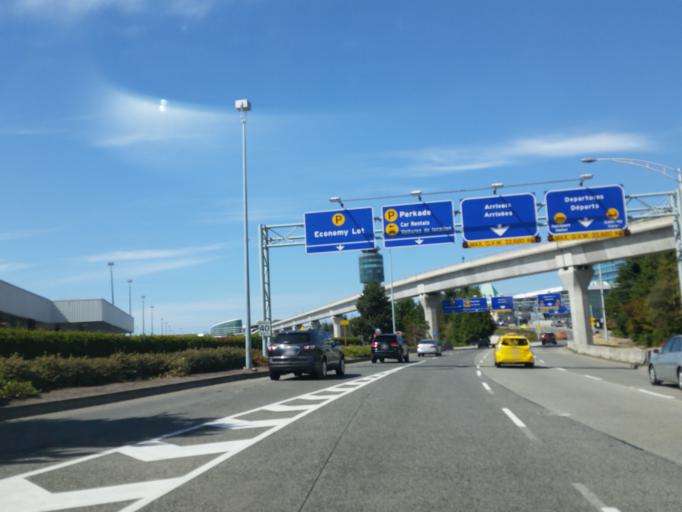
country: CA
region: British Columbia
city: Richmond
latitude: 49.1936
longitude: -123.1727
